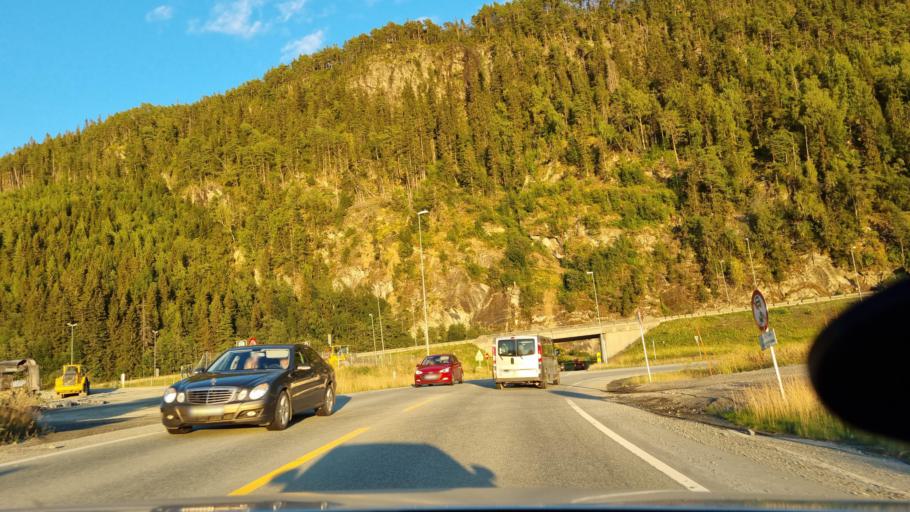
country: NO
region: Sor-Trondelag
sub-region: Malvik
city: Hommelvik
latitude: 63.4137
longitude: 10.8184
